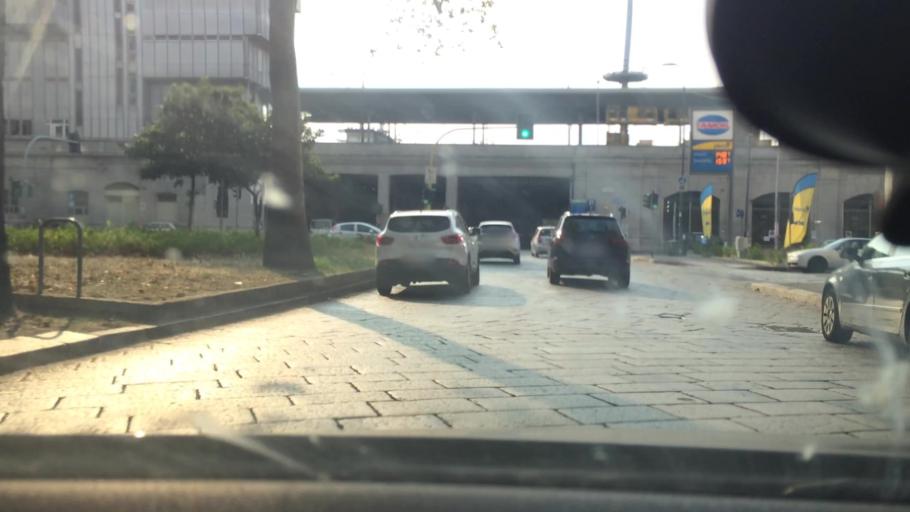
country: IT
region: Lombardy
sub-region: Citta metropolitana di Milano
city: Milano
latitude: 45.4907
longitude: 9.2065
